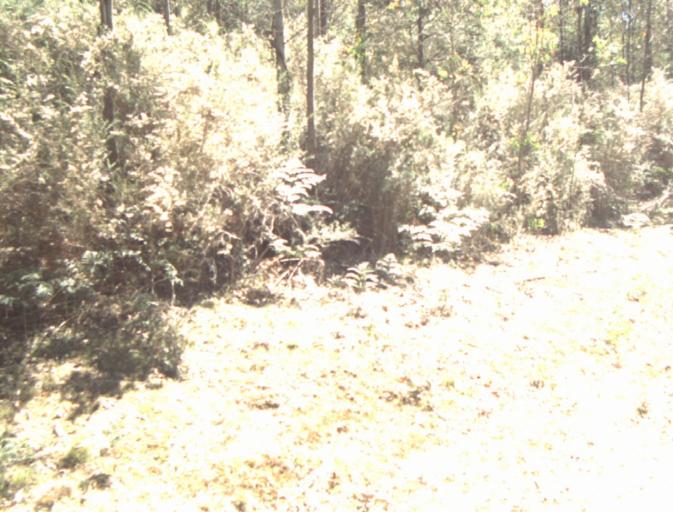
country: AU
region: Tasmania
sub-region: Dorset
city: Scottsdale
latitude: -41.3780
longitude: 147.4792
